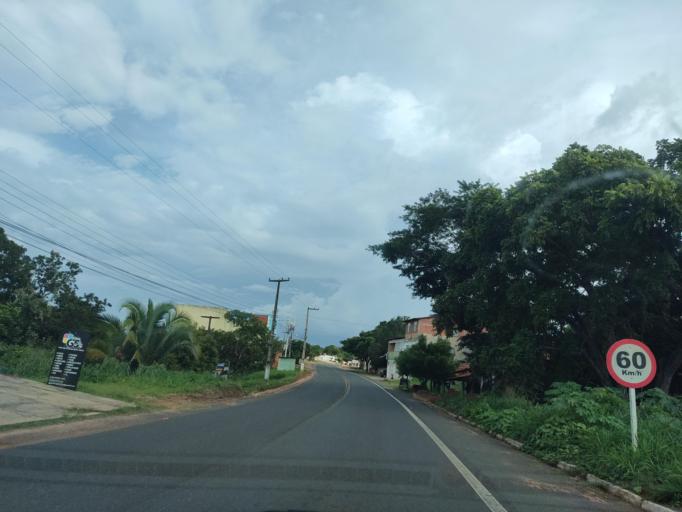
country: BR
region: Piaui
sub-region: Agua Branca
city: Agua Branca
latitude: -5.8206
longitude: -42.5088
